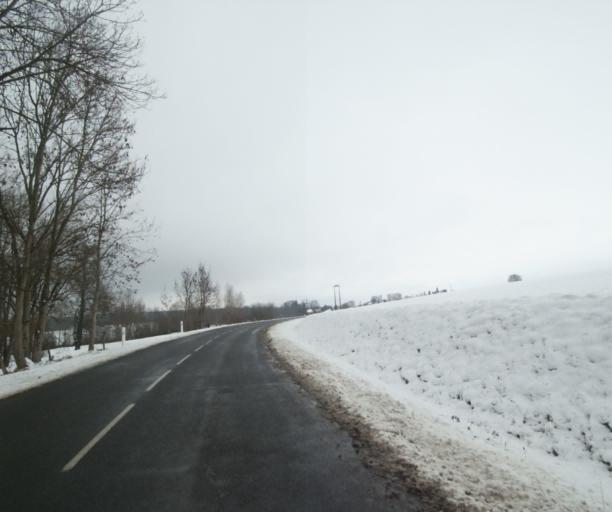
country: FR
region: Champagne-Ardenne
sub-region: Departement de la Haute-Marne
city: Wassy
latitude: 48.4419
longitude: 4.9555
